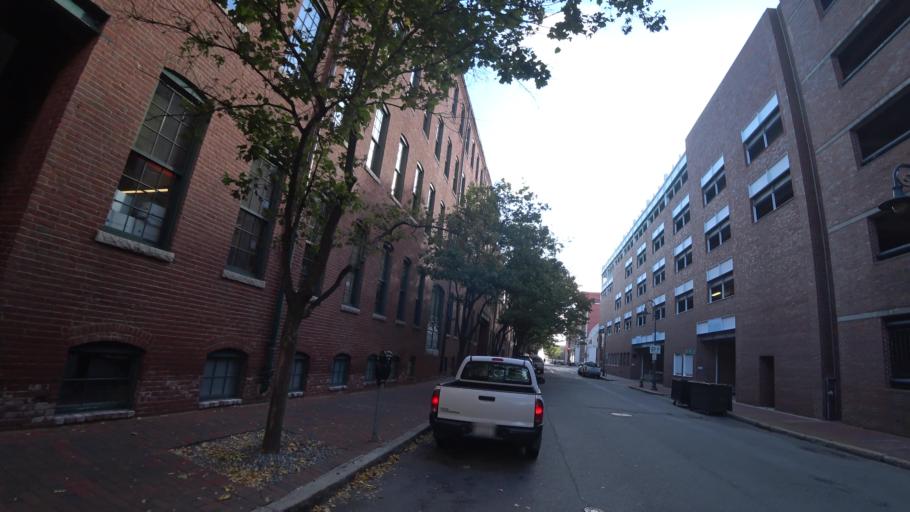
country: US
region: Massachusetts
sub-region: Suffolk County
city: Boston
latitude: 42.3694
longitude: -71.0782
